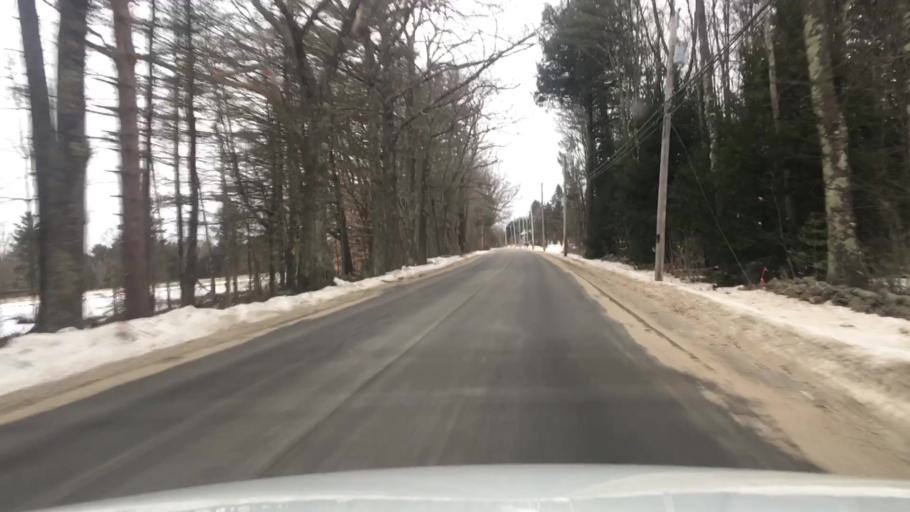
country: US
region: Maine
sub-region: York County
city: Shapleigh
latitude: 43.5262
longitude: -70.8456
